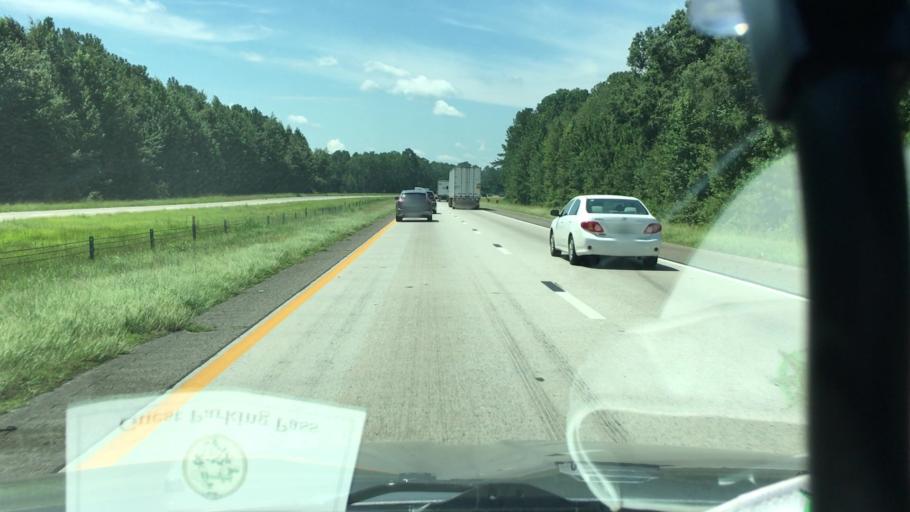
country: US
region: South Carolina
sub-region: Jasper County
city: Hardeeville
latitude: 32.2883
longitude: -81.0669
